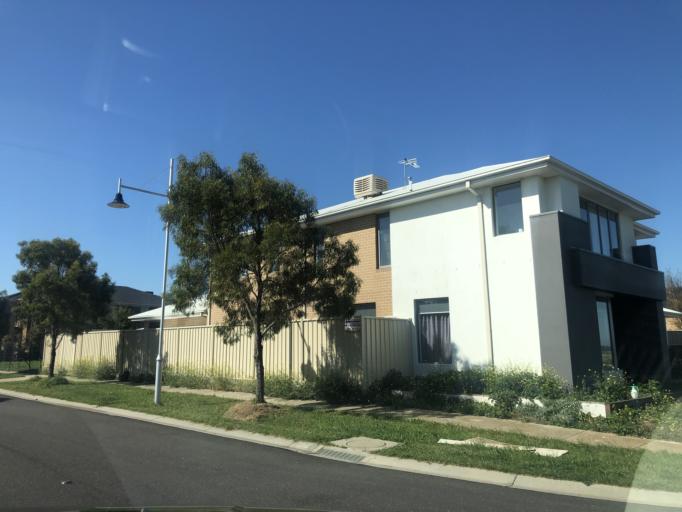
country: AU
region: Victoria
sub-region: Wyndham
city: Point Cook
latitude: -37.9117
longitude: 144.7253
